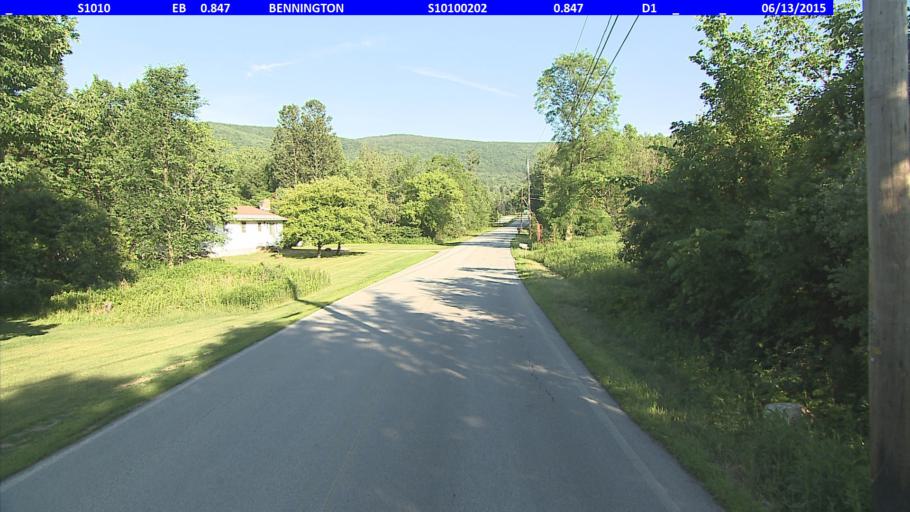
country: US
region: Vermont
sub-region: Bennington County
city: Bennington
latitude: 42.8765
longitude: -73.1596
